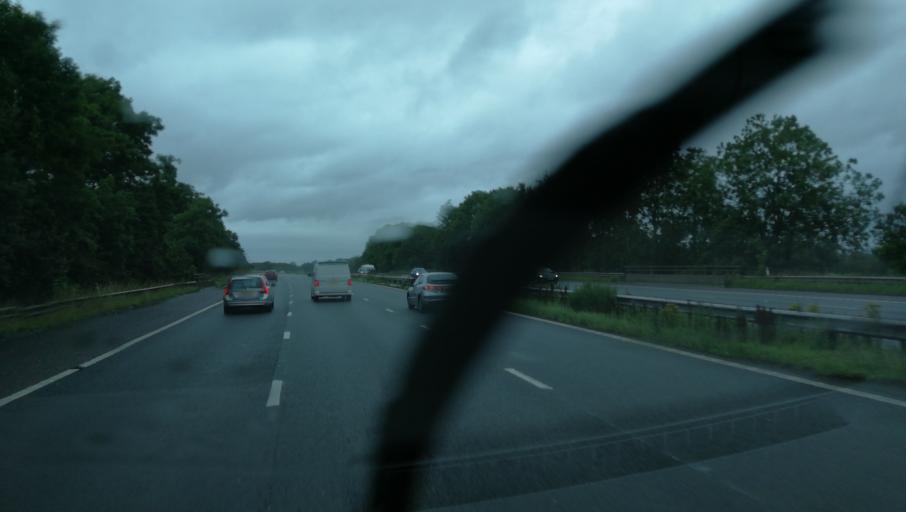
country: GB
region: England
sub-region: Borough of Bolton
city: Blackrod
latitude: 53.5915
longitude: -2.5637
